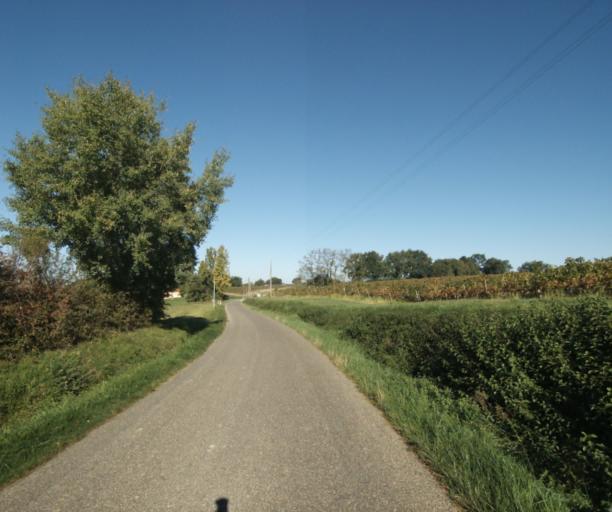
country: FR
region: Midi-Pyrenees
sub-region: Departement du Gers
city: Gondrin
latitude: 43.8226
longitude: 0.2170
